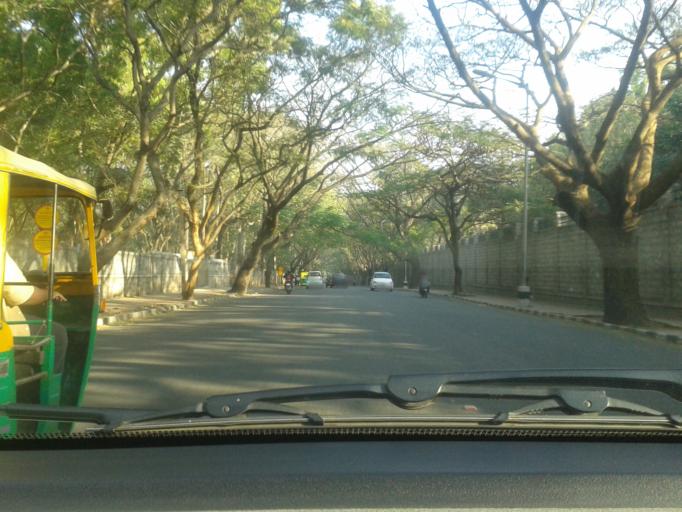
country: IN
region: Karnataka
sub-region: Bangalore Urban
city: Bangalore
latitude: 13.0195
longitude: 77.5724
